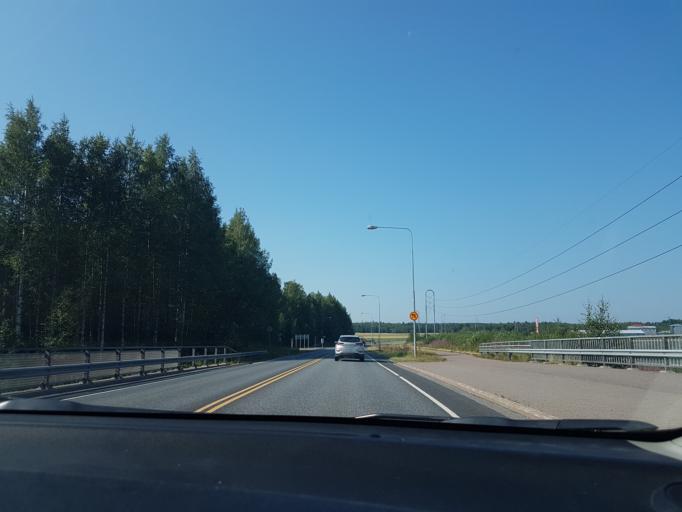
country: FI
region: Uusimaa
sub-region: Helsinki
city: Tuusula
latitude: 60.3775
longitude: 25.0542
